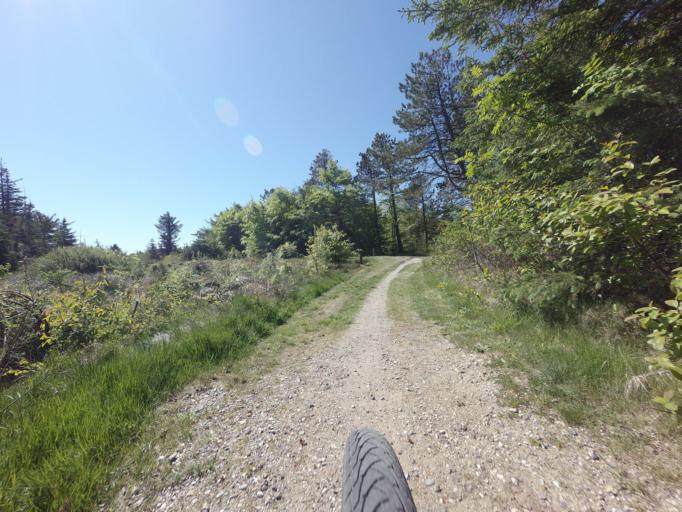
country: DK
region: North Denmark
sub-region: Jammerbugt Kommune
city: Pandrup
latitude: 57.2870
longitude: 9.6407
